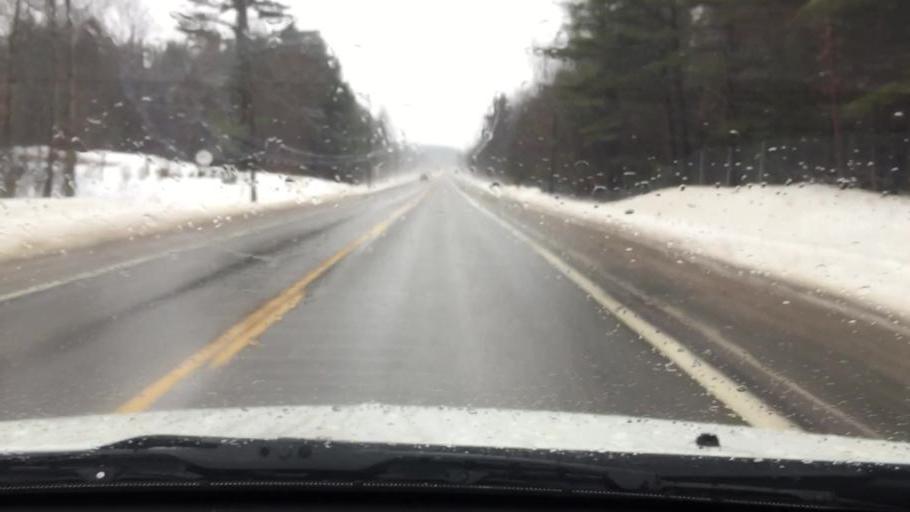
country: US
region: Michigan
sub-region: Charlevoix County
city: East Jordan
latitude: 45.2288
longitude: -85.1817
